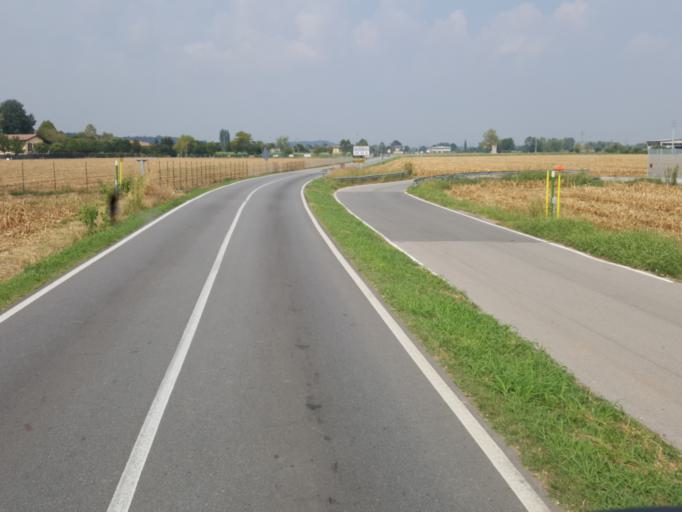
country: IT
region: Lombardy
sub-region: Provincia di Brescia
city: Carpenedolo
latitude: 45.3801
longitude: 10.4112
